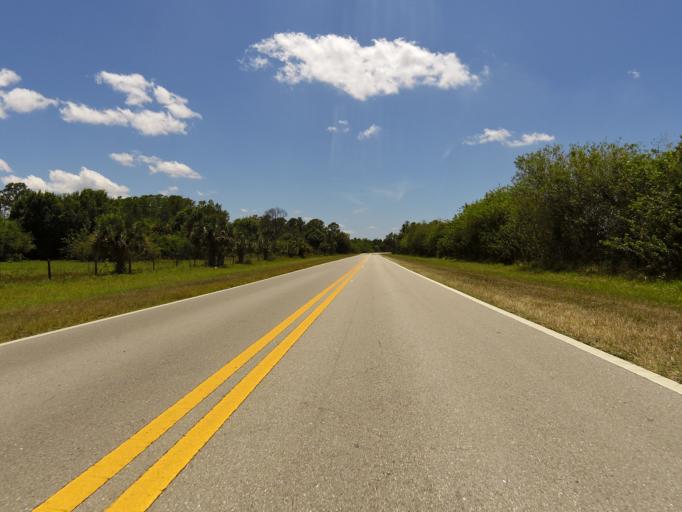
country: US
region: Florida
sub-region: Collier County
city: Immokalee
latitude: 26.3001
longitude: -81.3583
